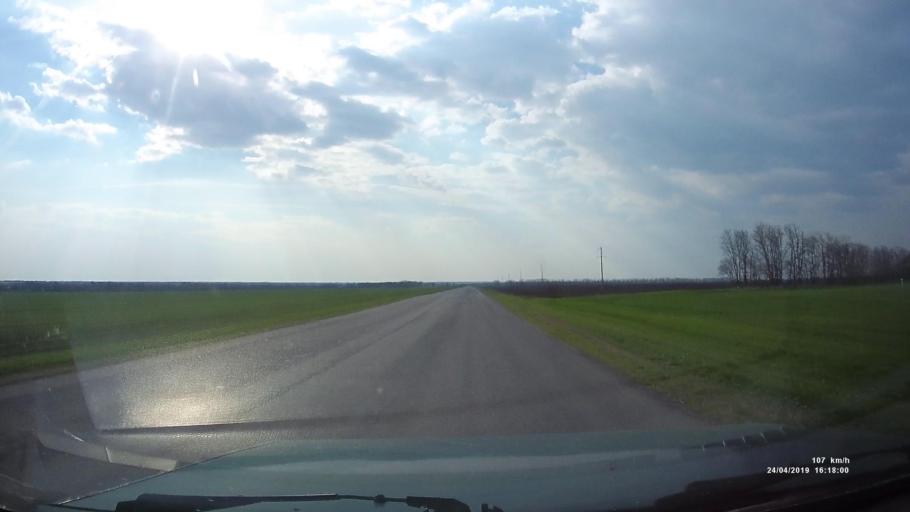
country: RU
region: Rostov
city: Sovetskoye
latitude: 46.7720
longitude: 42.1258
